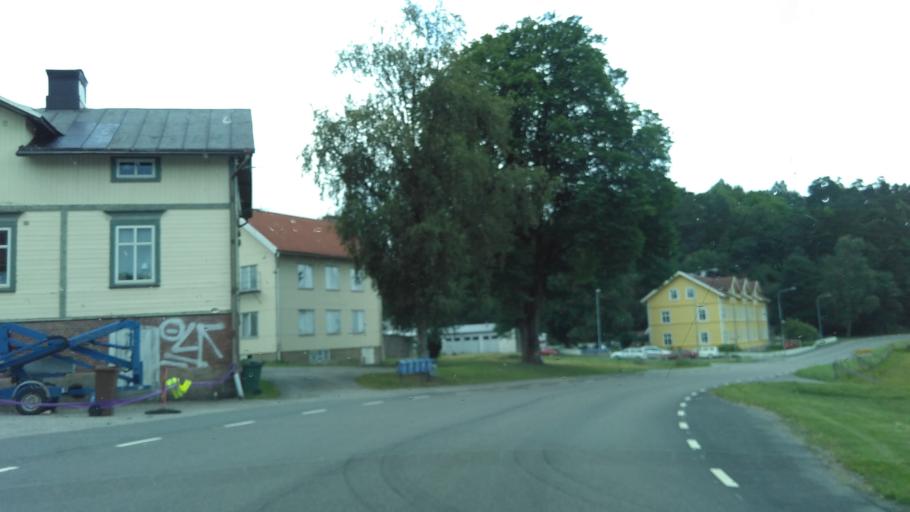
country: SE
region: Vaestra Goetaland
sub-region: Marks Kommun
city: Fritsla
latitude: 57.5581
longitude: 12.7846
